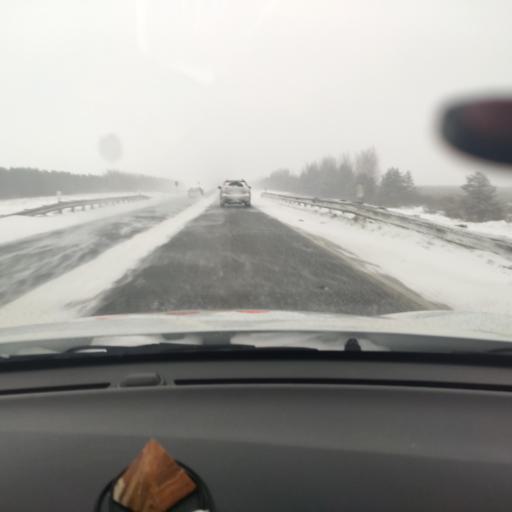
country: RU
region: Tatarstan
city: Verkhniy Uslon
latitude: 55.6653
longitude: 48.8623
